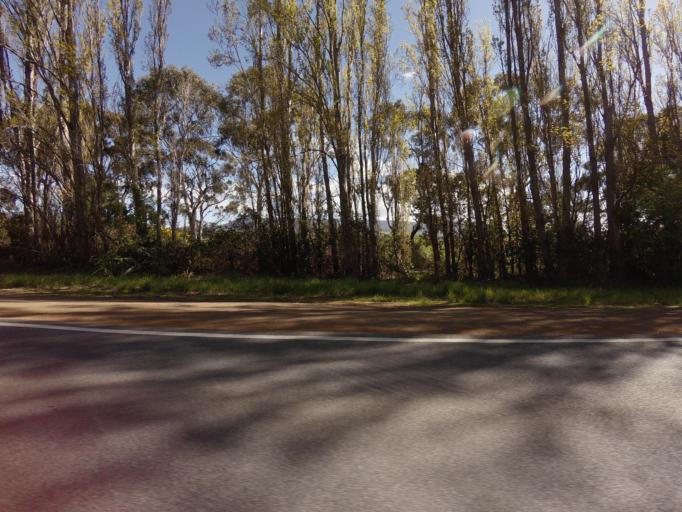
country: AU
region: Tasmania
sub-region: Derwent Valley
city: New Norfolk
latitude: -42.7361
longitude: 146.9764
